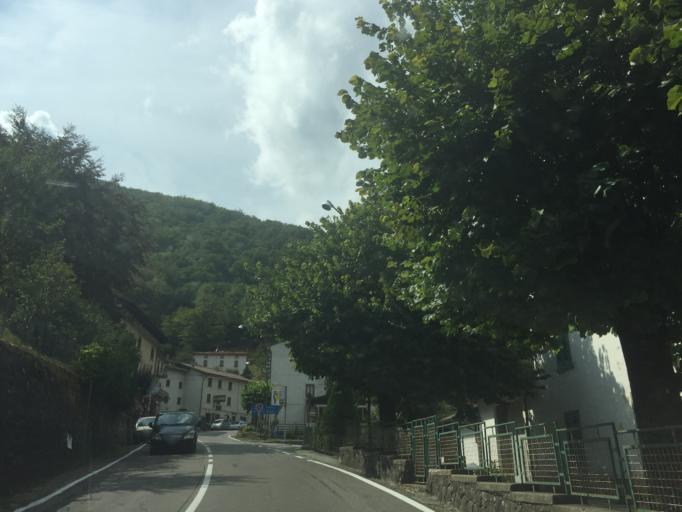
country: IT
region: Tuscany
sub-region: Provincia di Pistoia
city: Cutigliano
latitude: 44.1199
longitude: 10.7286
